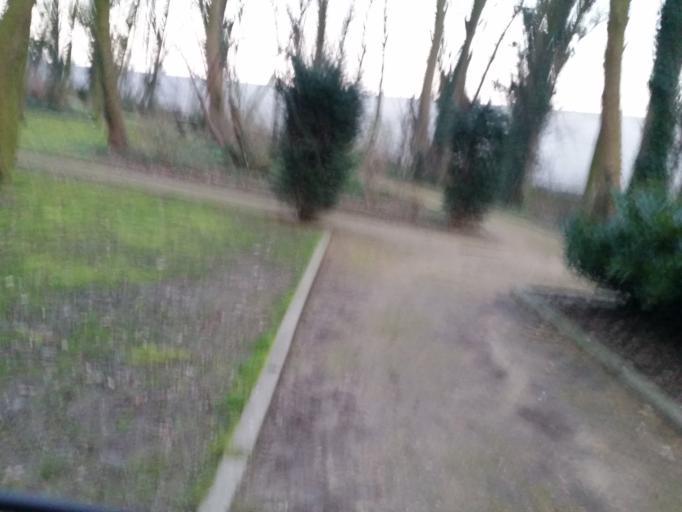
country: BE
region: Flanders
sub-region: Provincie Vlaams-Brabant
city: Diegem
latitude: 50.8935
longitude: 4.3927
